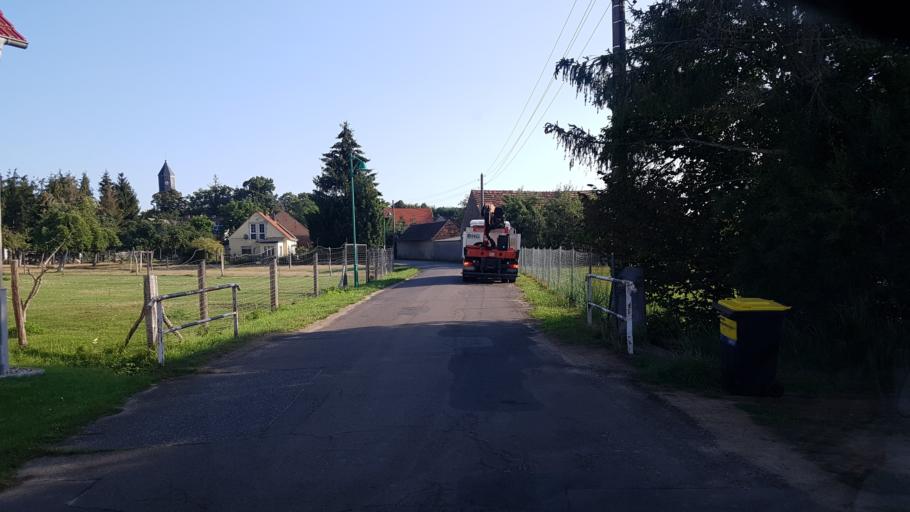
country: DE
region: Brandenburg
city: Luckau
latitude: 51.8014
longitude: 13.6487
